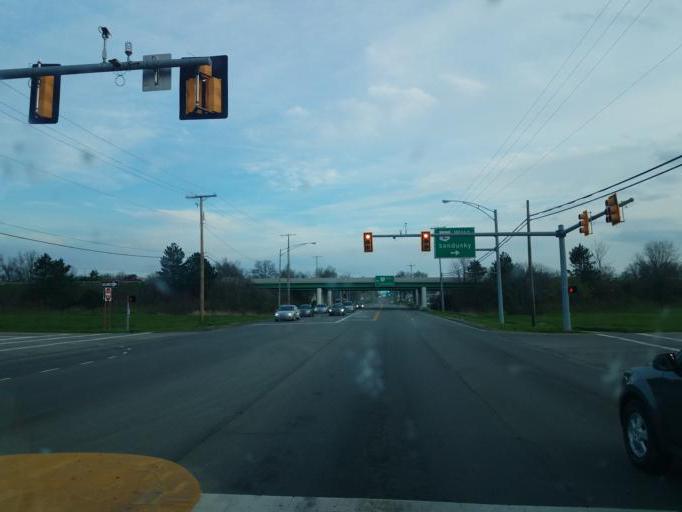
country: US
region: Ohio
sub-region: Lorain County
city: Amherst
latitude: 41.4152
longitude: -82.2089
